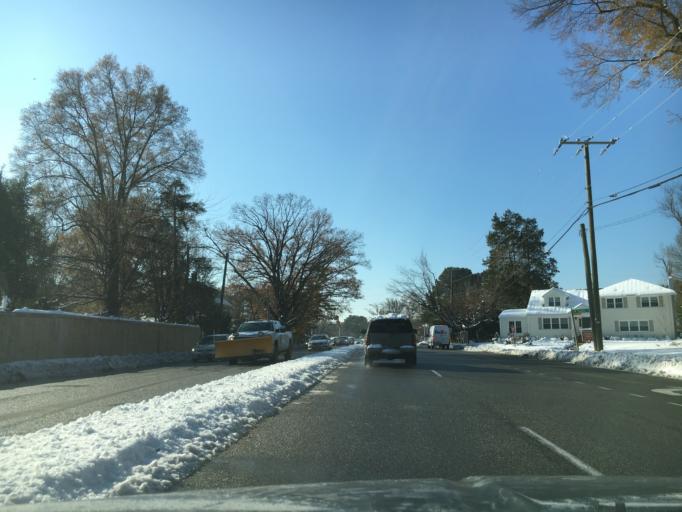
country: US
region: Virginia
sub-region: Henrico County
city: Tuckahoe
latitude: 37.5956
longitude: -77.5311
